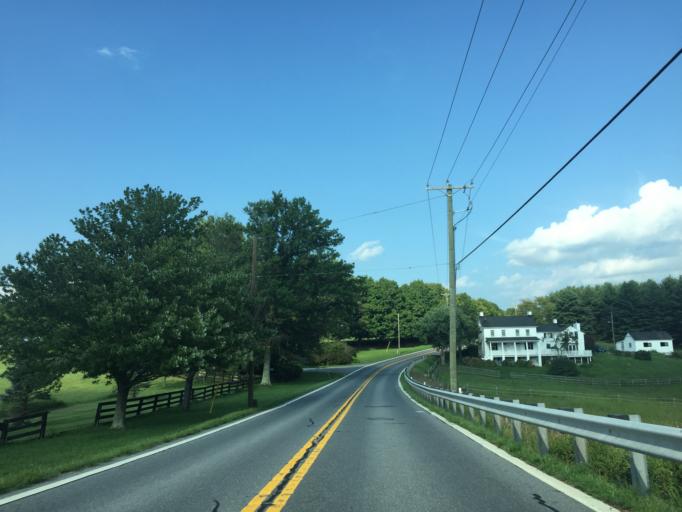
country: US
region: Maryland
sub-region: Carroll County
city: Hampstead
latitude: 39.5931
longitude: -76.7418
